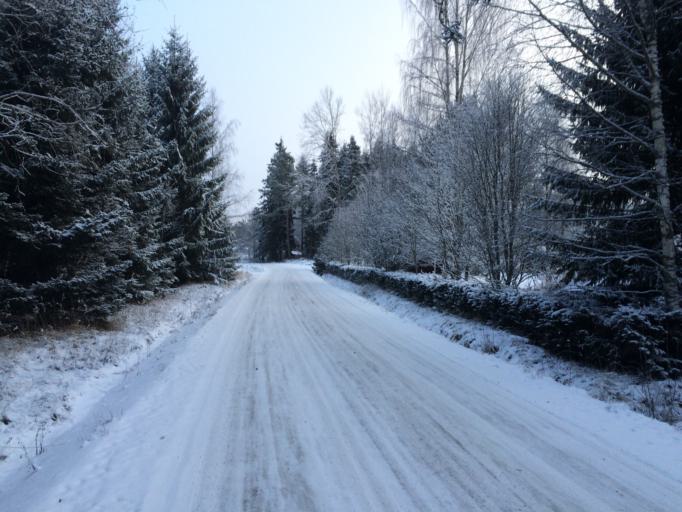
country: SE
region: Uppsala
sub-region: Enkopings Kommun
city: Orsundsbro
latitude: 59.9088
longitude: 17.1982
